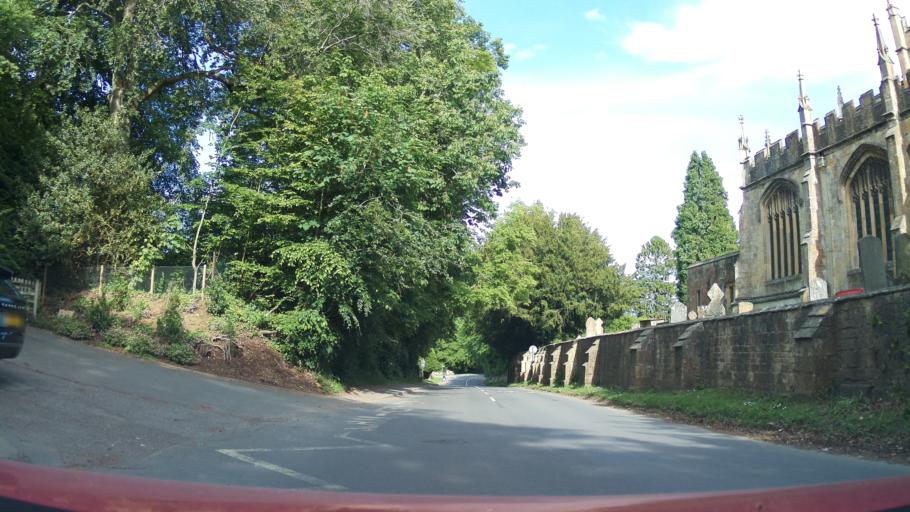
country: GB
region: England
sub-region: Gloucestershire
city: Chipping Campden
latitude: 52.0535
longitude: -1.7764
